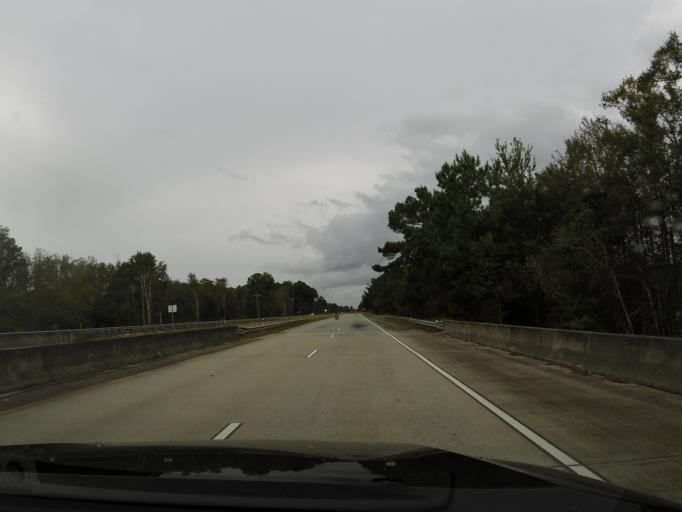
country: US
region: Georgia
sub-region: McIntosh County
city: Darien
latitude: 31.3824
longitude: -81.6352
